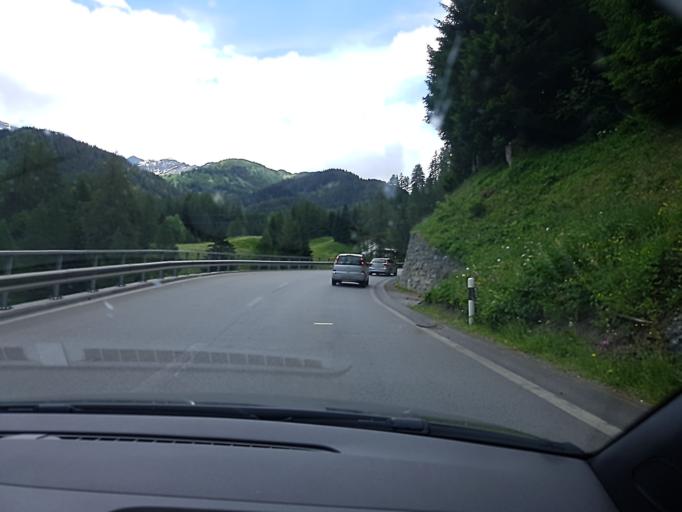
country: CH
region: Grisons
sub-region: Albula District
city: Tiefencastel
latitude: 46.5221
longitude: 9.6212
